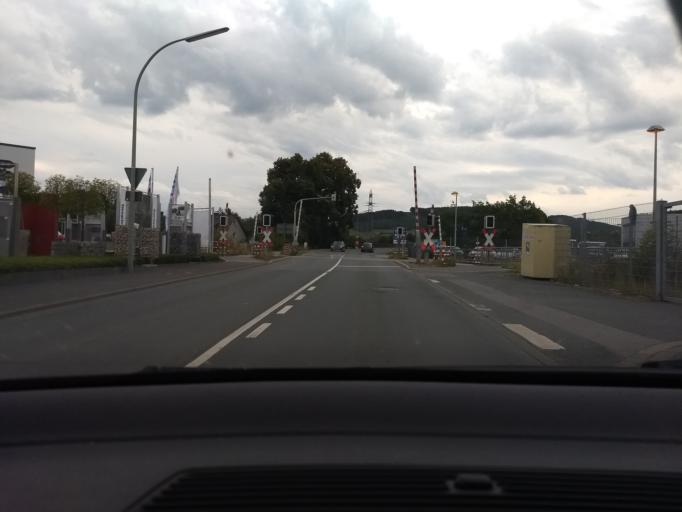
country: DE
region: North Rhine-Westphalia
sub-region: Regierungsbezirk Arnsberg
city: Arnsberg
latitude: 51.3648
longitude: 8.1722
